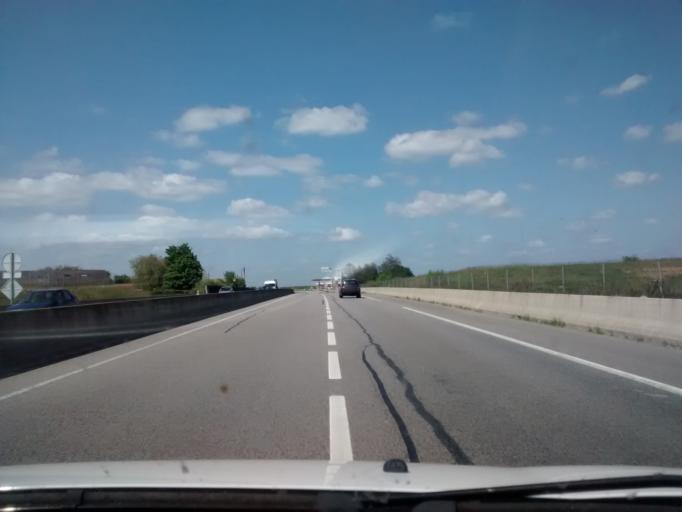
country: FR
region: Ile-de-France
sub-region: Departement des Yvelines
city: Sonchamp
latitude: 48.5643
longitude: 1.8325
